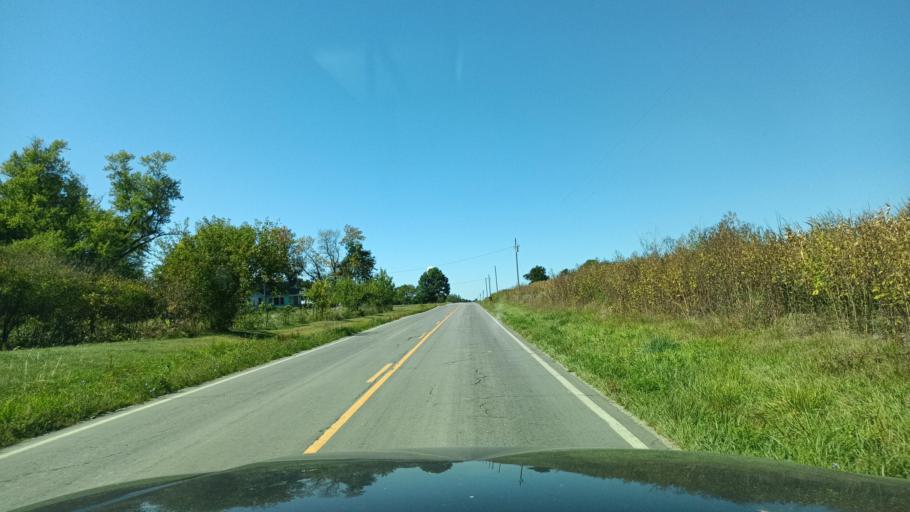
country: US
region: Missouri
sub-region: Macon County
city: La Plata
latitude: 40.0216
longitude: -92.5216
